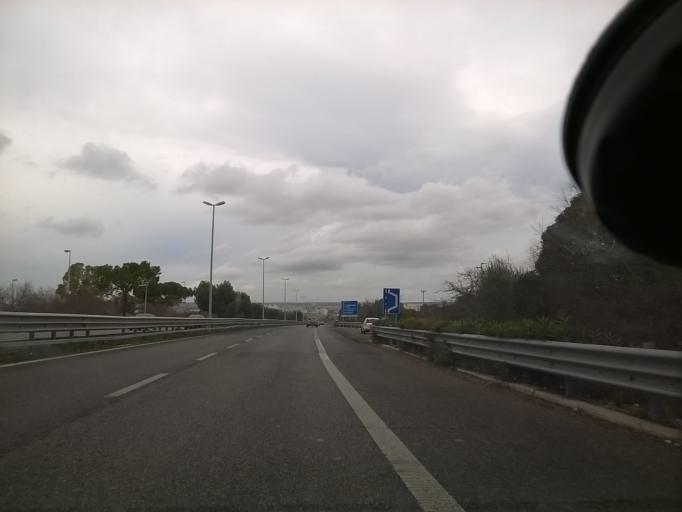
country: IT
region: Apulia
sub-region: Provincia di Taranto
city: Paolo VI
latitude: 40.4905
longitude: 17.2676
